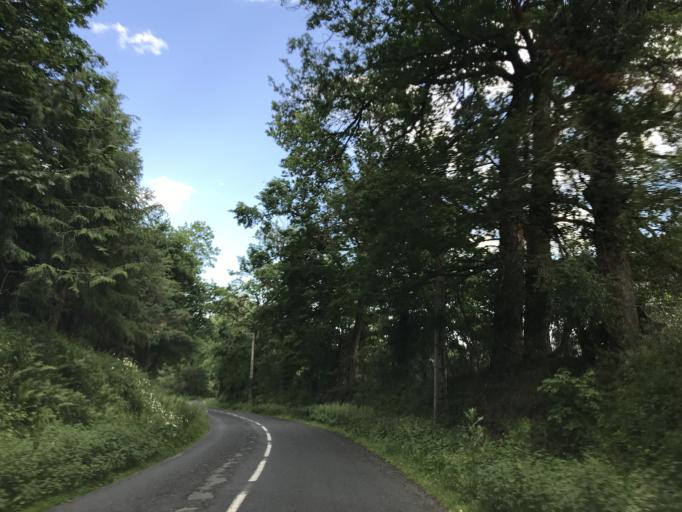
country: FR
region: Auvergne
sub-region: Departement du Puy-de-Dome
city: Courpiere
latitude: 45.7711
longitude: 3.5990
